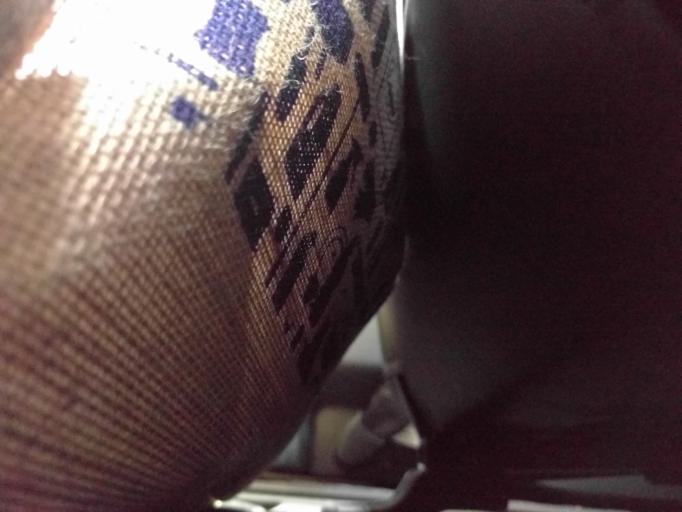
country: AE
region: Abu Dhabi
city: Abu Dhabi
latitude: 24.4452
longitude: 54.4026
